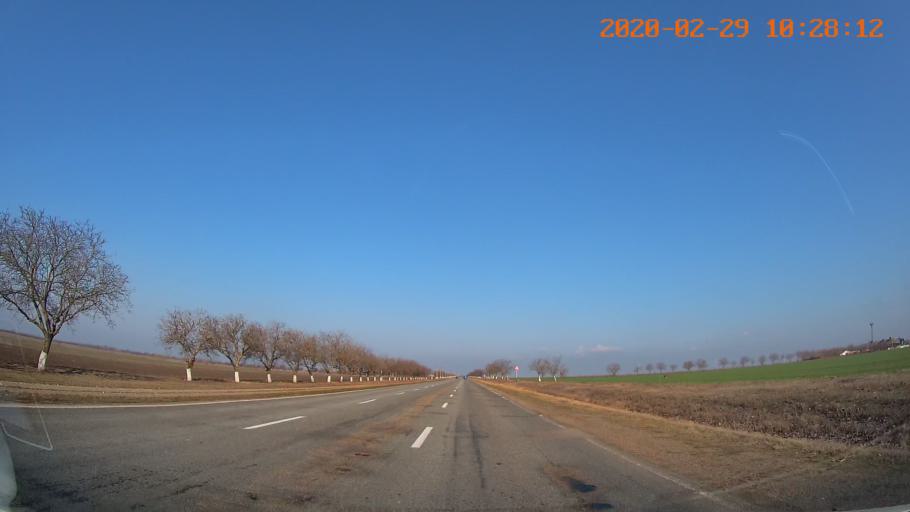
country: MD
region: Telenesti
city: Tiraspolul Nou
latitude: 46.9072
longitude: 29.5929
